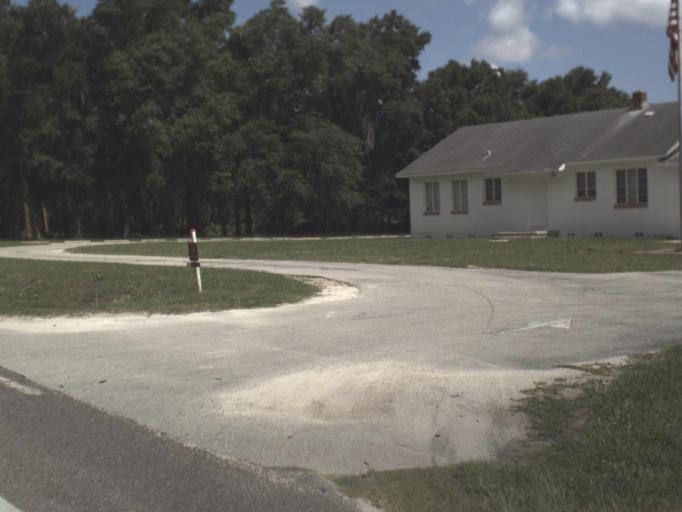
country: US
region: Florida
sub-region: Putnam County
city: East Palatka
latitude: 29.6018
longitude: -81.5821
